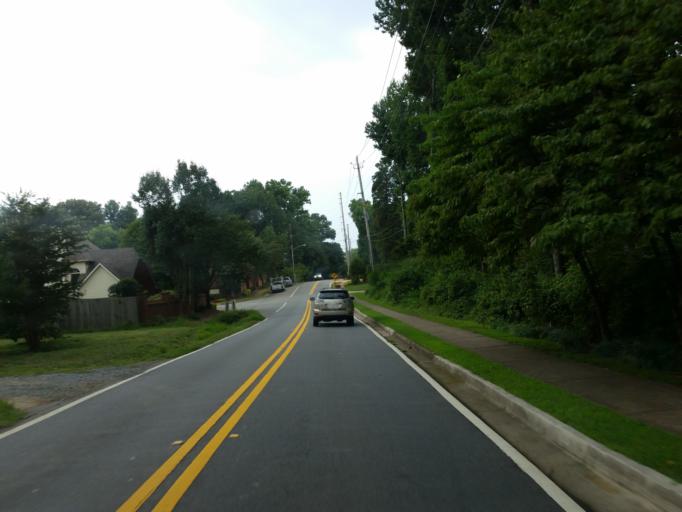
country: US
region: Georgia
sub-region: Fulton County
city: Sandy Springs
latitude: 33.9625
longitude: -84.4161
